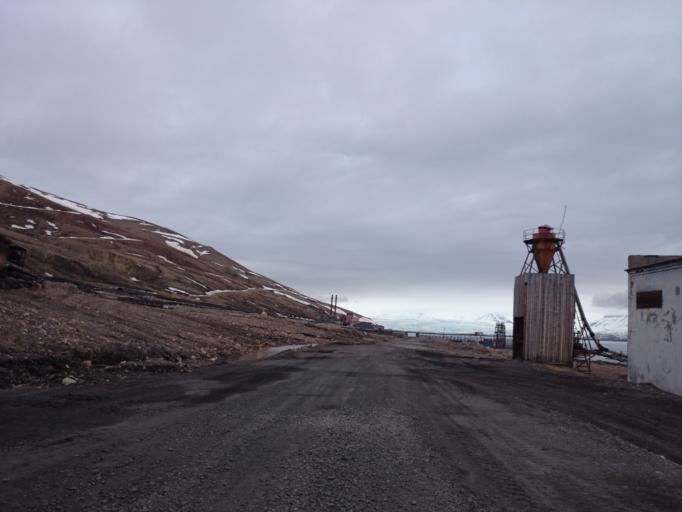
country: SJ
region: Svalbard
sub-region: Spitsbergen
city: Longyearbyen
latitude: 78.6554
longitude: 16.3575
